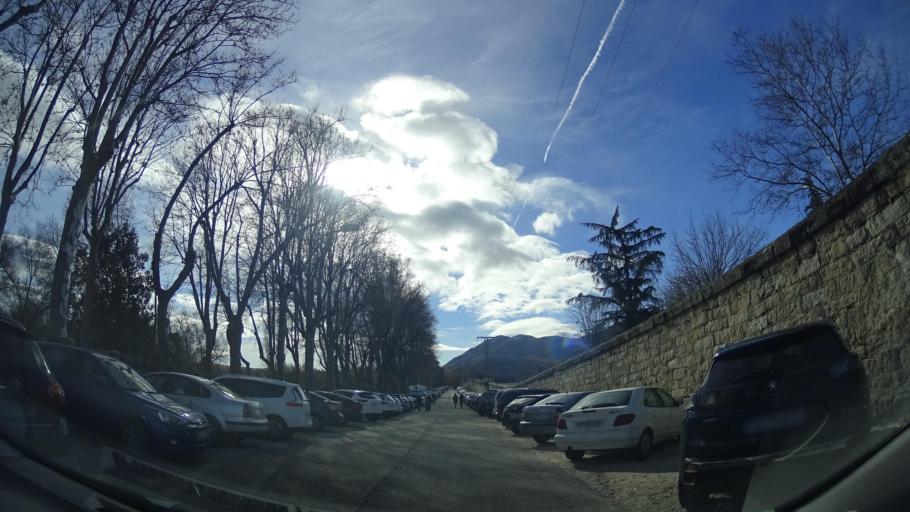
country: ES
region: Madrid
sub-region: Provincia de Madrid
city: San Lorenzo de El Escorial
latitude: 40.5875
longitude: -4.1437
